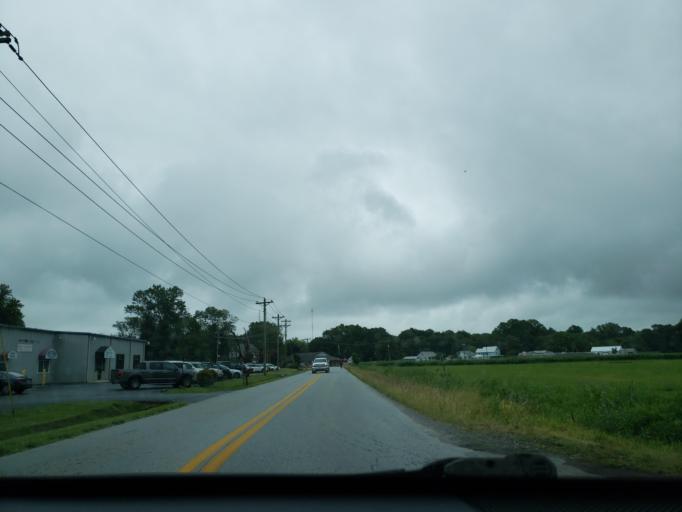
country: US
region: Delaware
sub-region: Sussex County
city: Lewes
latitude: 38.7508
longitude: -75.1616
